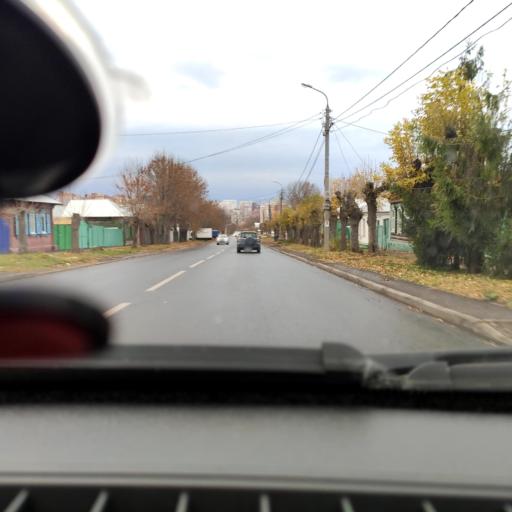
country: RU
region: Bashkortostan
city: Ufa
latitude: 54.7218
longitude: 55.9691
